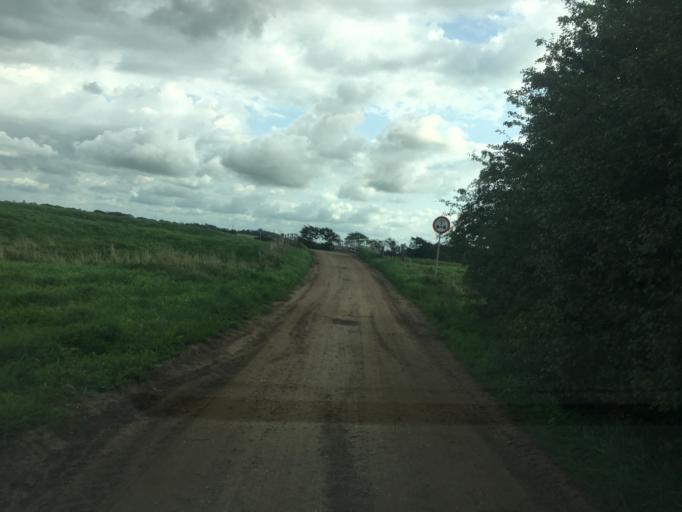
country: DK
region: South Denmark
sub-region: Tonder Kommune
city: Tonder
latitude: 54.9464
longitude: 8.9058
